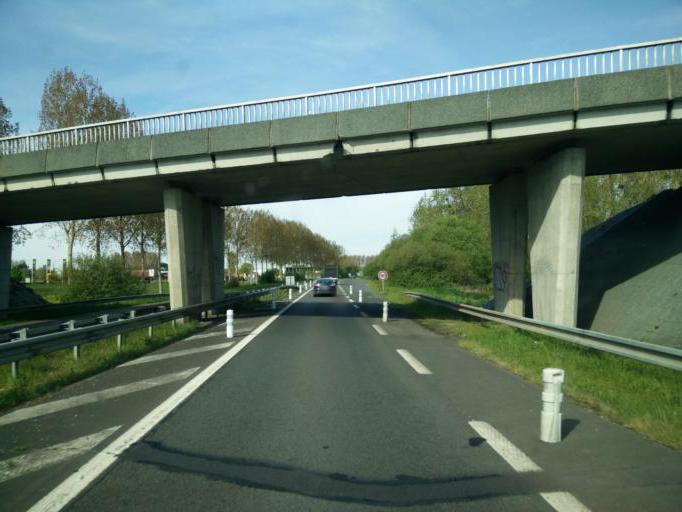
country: FR
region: Lower Normandy
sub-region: Departement de la Manche
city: Pontorson
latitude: 48.5610
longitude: -1.4862
